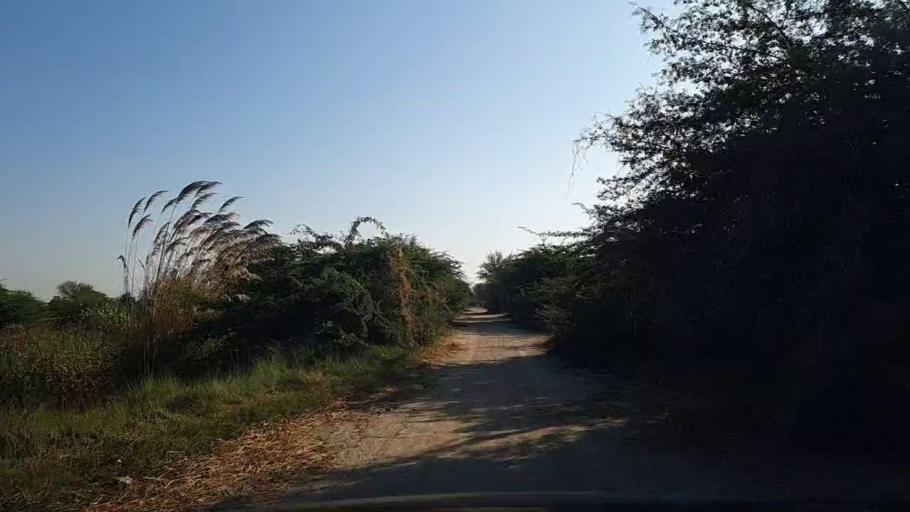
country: PK
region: Sindh
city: Mirpur Batoro
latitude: 24.6744
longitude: 68.3644
